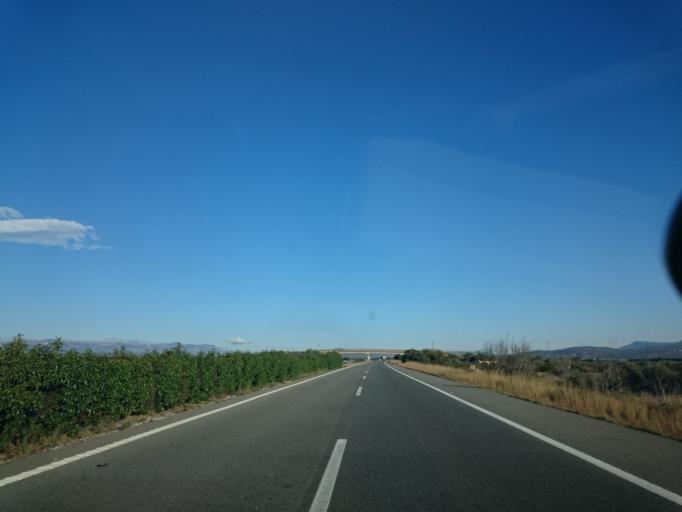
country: ES
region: Catalonia
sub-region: Provincia de Tarragona
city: Alcanar
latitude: 40.5223
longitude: 0.4166
